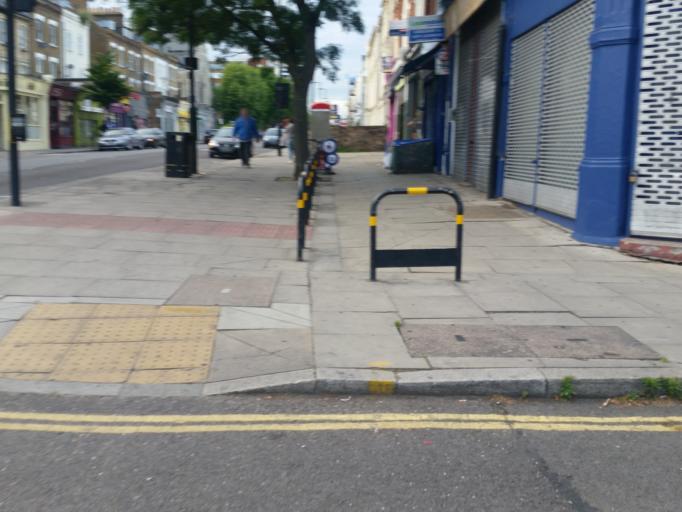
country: GB
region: England
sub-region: Greater London
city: Holloway
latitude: 51.5602
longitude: -0.1370
